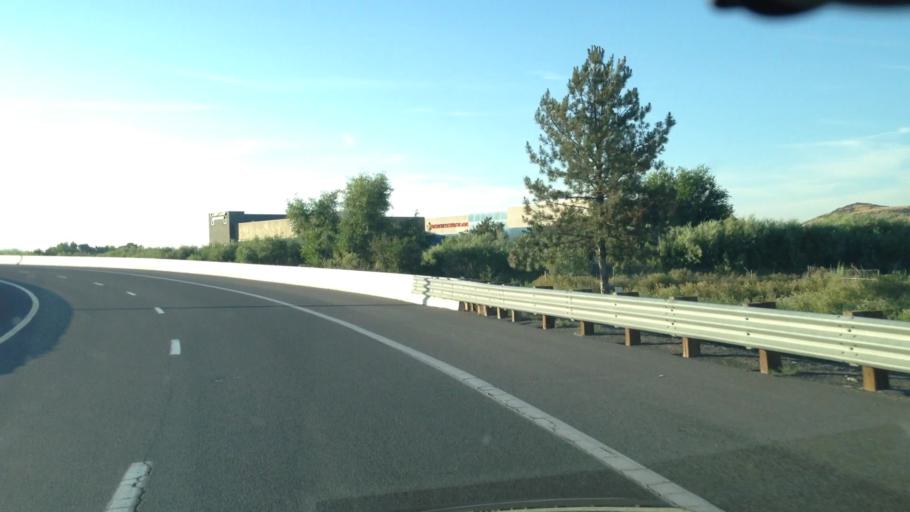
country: US
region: Nevada
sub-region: Washoe County
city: Sparks
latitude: 39.4398
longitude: -119.7638
